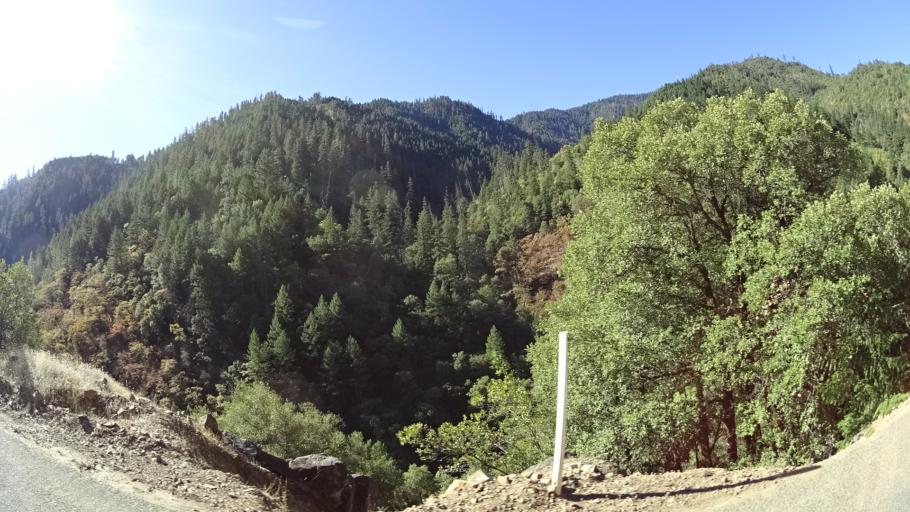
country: US
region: California
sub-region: Humboldt County
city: Willow Creek
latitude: 41.1690
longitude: -123.2178
